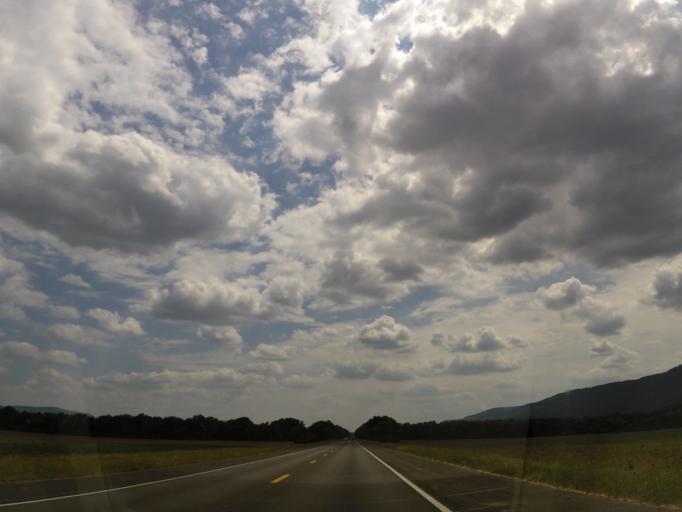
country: US
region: Tennessee
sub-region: Marion County
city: Powells Crossroads
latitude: 35.2405
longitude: -85.4846
